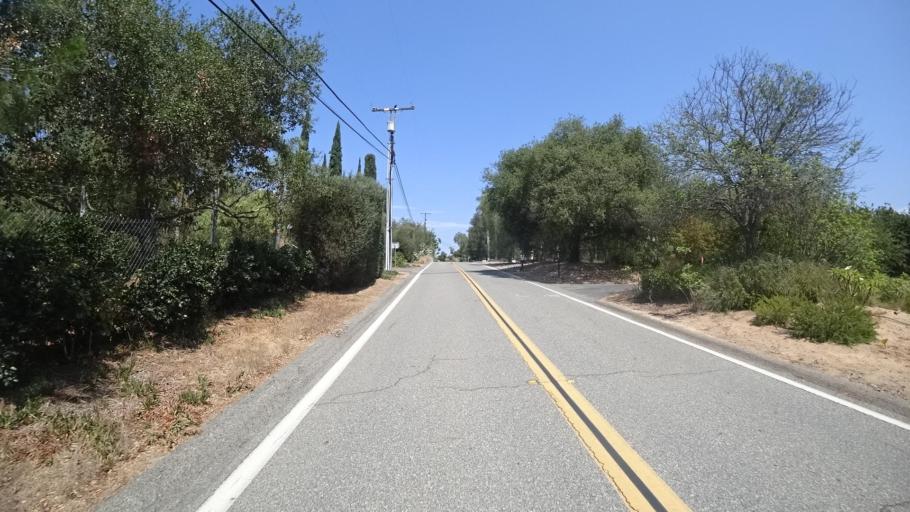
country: US
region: California
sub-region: San Diego County
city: Fallbrook
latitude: 33.3419
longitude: -117.2218
